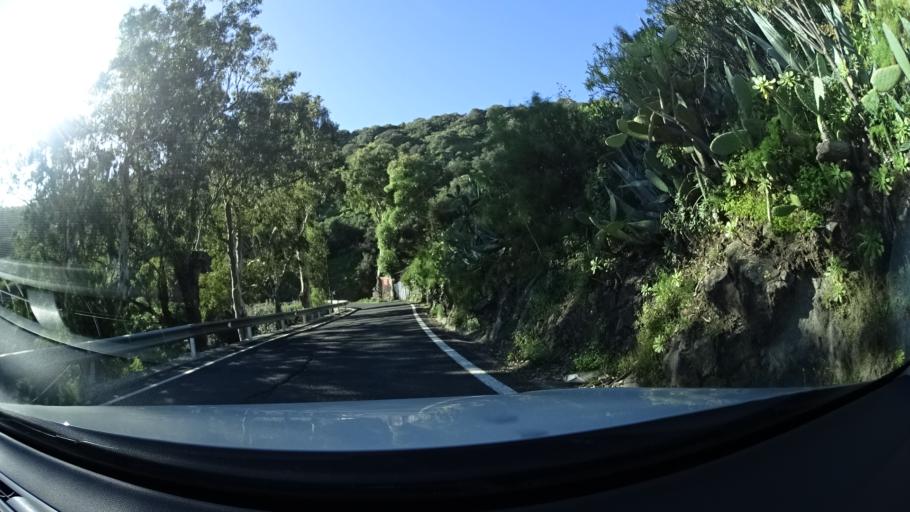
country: ES
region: Canary Islands
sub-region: Provincia de Las Palmas
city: Santa Brigida
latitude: 28.0194
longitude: -15.4670
